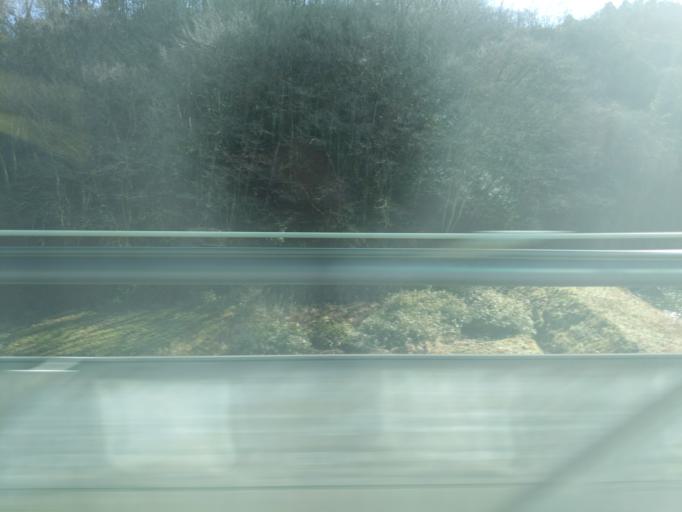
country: JP
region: Miyagi
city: Okawara
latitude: 38.0999
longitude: 140.7661
